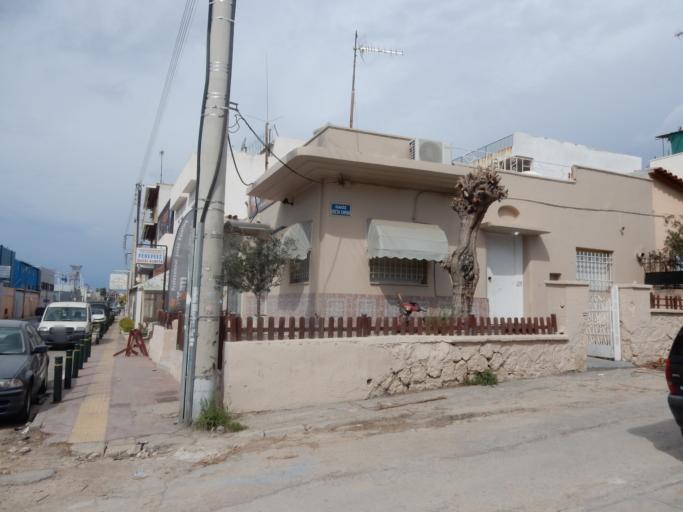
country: GR
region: Attica
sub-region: Nomos Piraios
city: Perama
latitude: 37.9631
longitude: 23.5724
